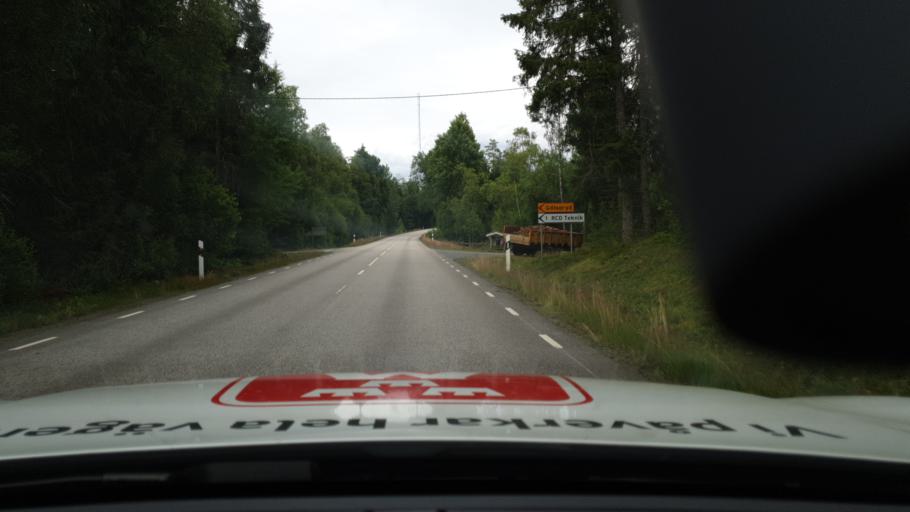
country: SE
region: Joenkoeping
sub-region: Varnamo Kommun
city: Varnamo
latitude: 57.1165
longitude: 13.9825
